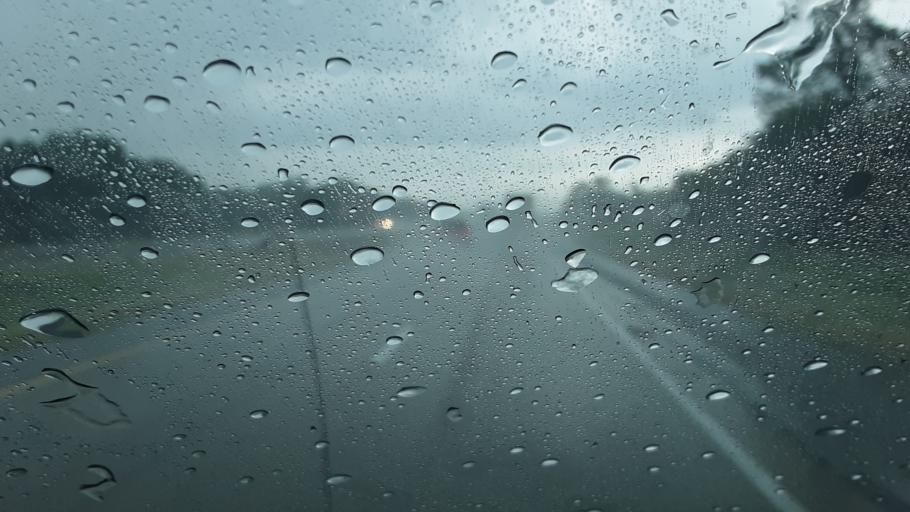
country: US
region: Iowa
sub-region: Pottawattamie County
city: Council Bluffs
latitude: 41.2971
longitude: -95.7736
